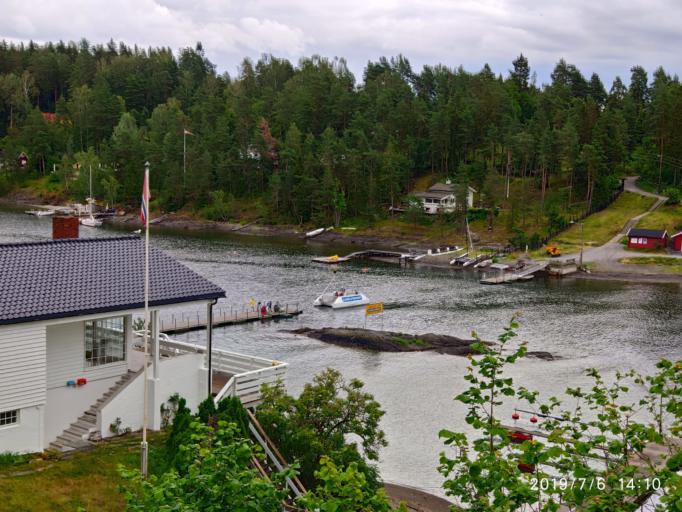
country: NO
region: Akershus
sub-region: Baerum
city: Sandvika
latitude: 59.8601
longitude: 10.5263
